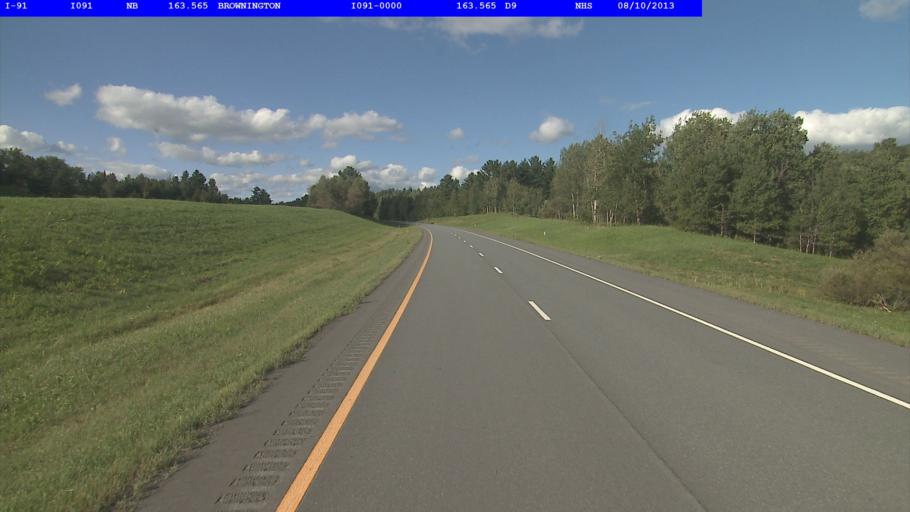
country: US
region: Vermont
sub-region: Orleans County
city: Newport
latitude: 44.8345
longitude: -72.1956
